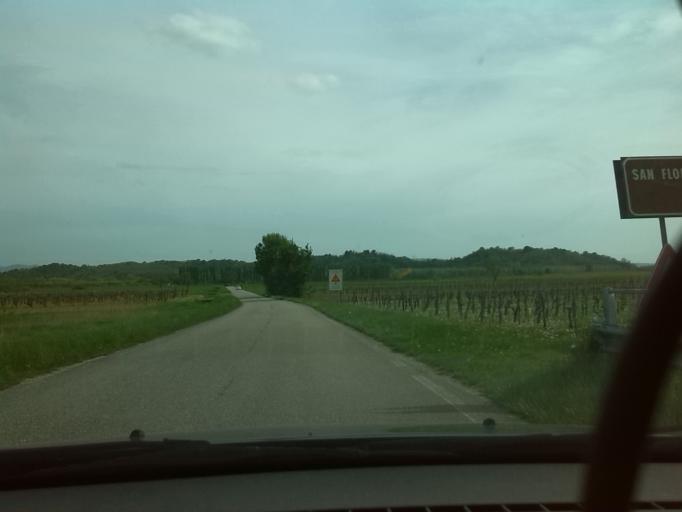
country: IT
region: Friuli Venezia Giulia
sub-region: Provincia di Gorizia
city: Capriva del Friuli
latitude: 45.9675
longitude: 13.5230
